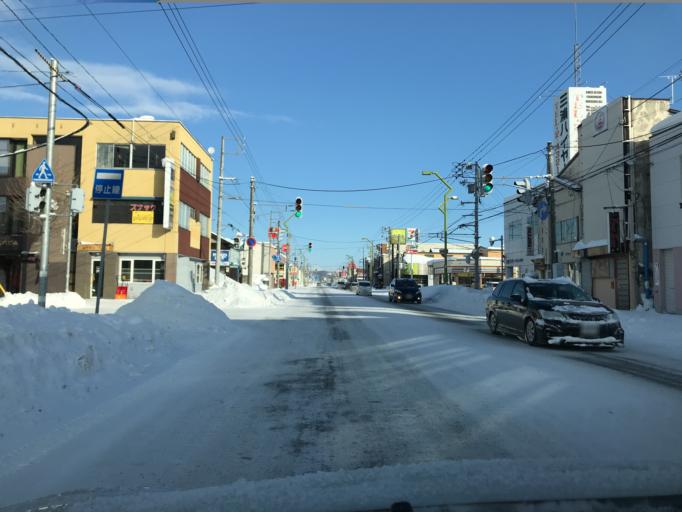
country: JP
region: Hokkaido
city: Nayoro
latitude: 44.3511
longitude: 142.4571
